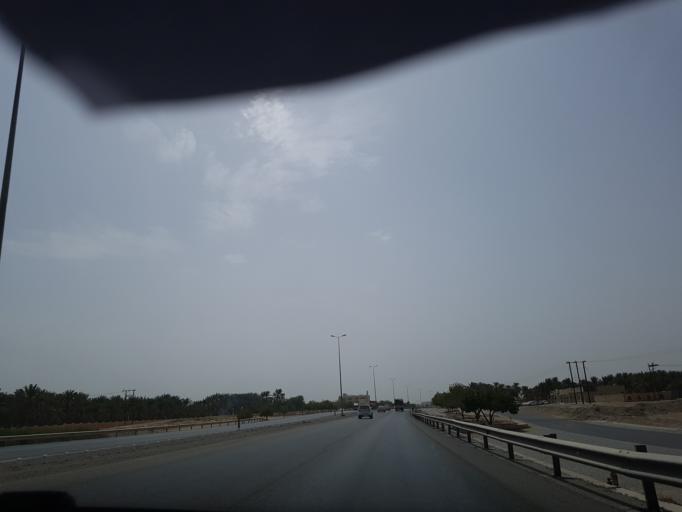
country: OM
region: Al Batinah
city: As Suwayq
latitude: 23.7519
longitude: 57.6114
